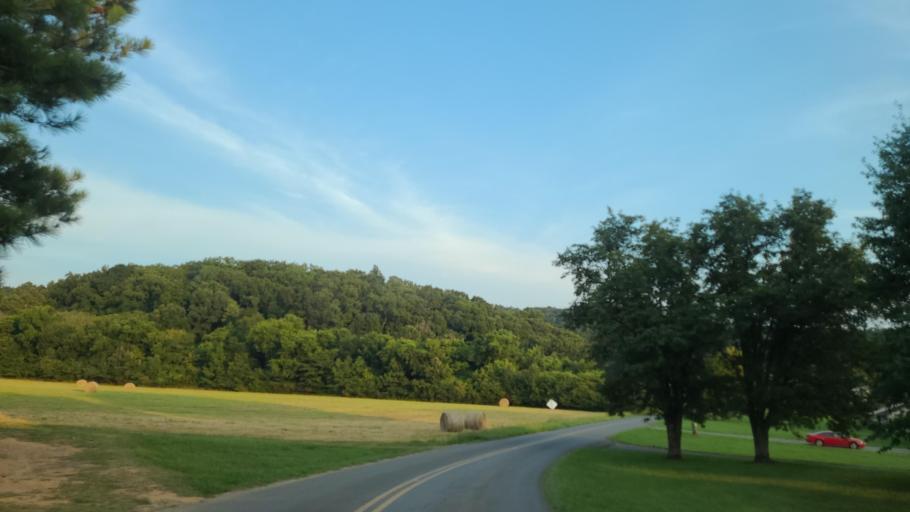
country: US
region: Georgia
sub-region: Bartow County
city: Adairsville
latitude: 34.4287
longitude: -84.9137
